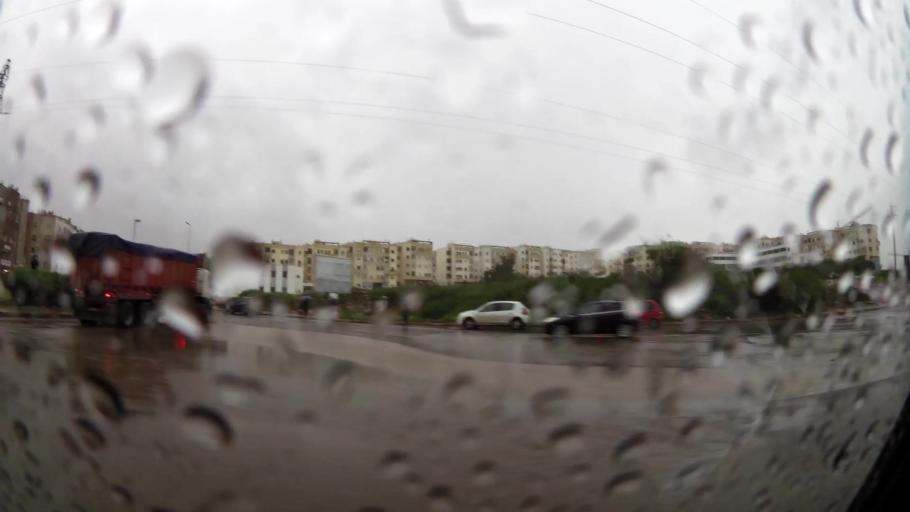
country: MA
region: Grand Casablanca
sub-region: Mediouna
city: Tit Mellil
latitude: 33.5887
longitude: -7.4991
